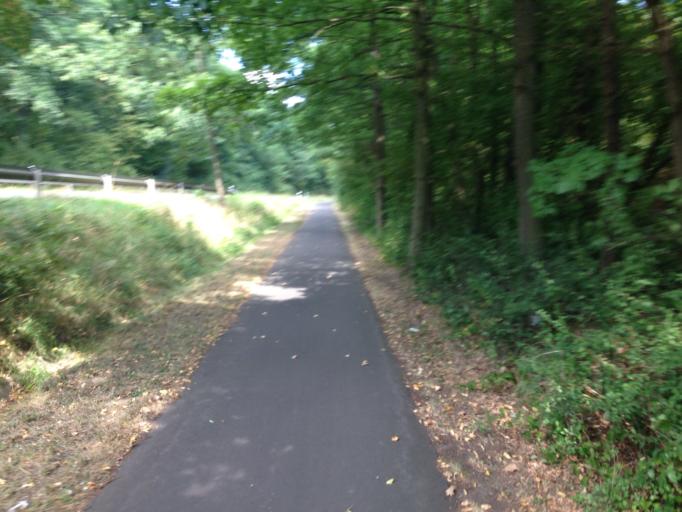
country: DE
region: Hesse
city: Allendorf an der Lahn
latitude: 50.5494
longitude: 8.6345
